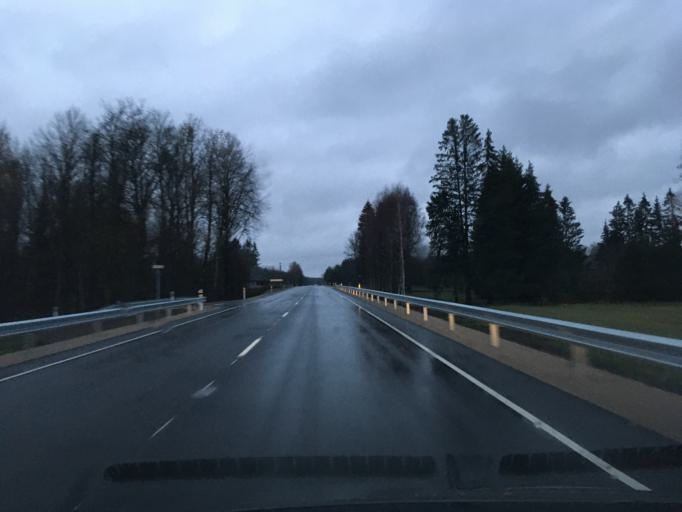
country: EE
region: Laeaene
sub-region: Lihula vald
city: Lihula
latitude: 58.6494
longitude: 23.7105
